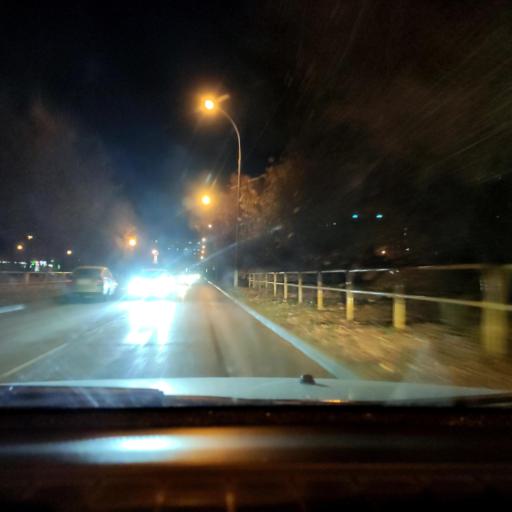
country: RU
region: Samara
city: Tol'yatti
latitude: 53.5366
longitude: 49.3213
